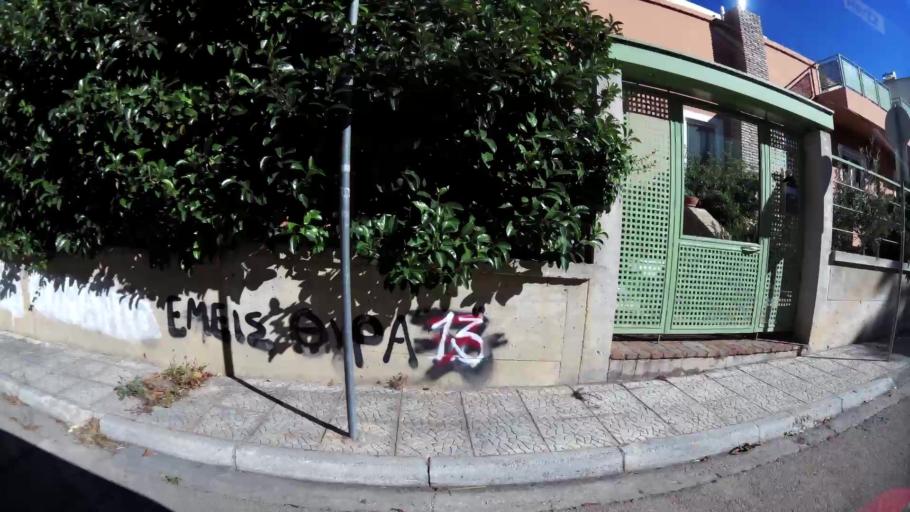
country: GR
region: Attica
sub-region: Nomarchia Anatolikis Attikis
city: Leondarion
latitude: 37.9872
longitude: 23.8480
